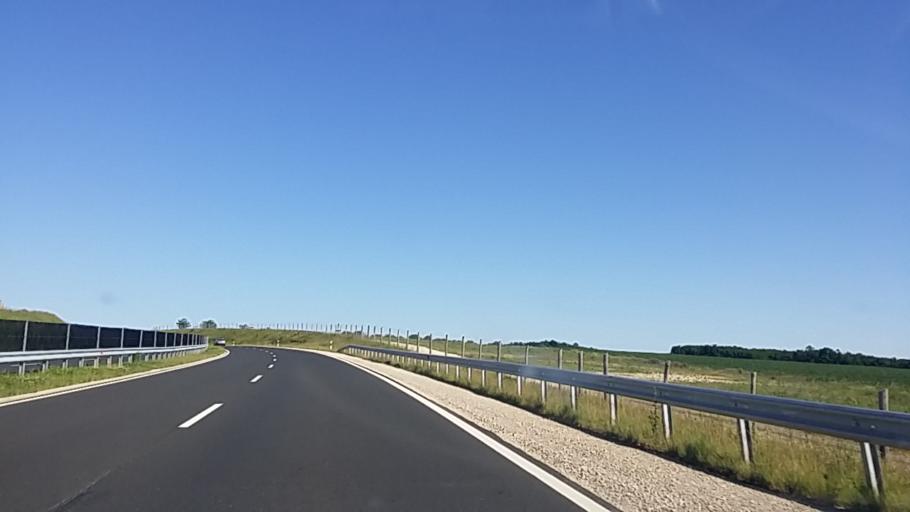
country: HU
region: Zala
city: Heviz
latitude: 46.7972
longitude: 17.1560
